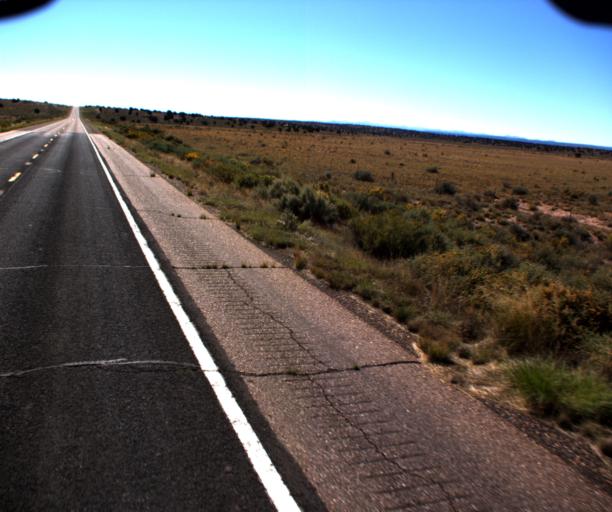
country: US
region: Arizona
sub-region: Navajo County
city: Snowflake
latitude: 34.6681
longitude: -109.7223
